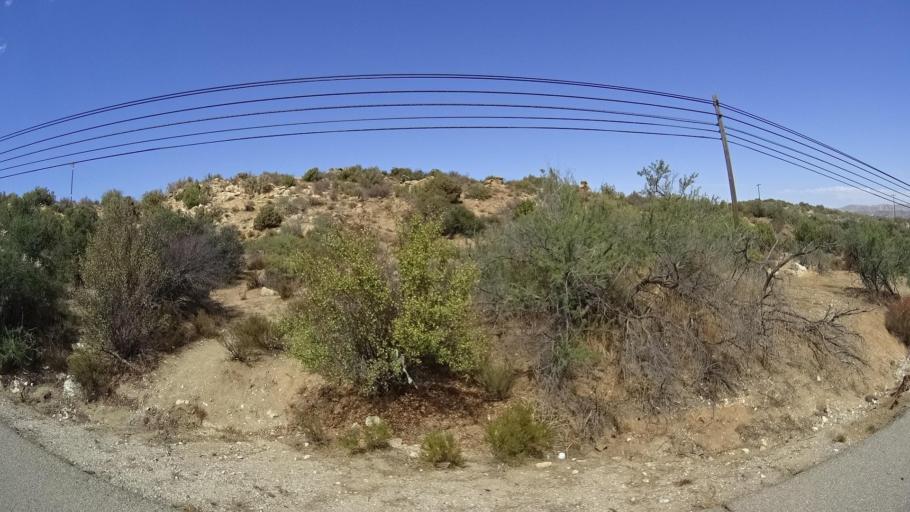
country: MX
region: Baja California
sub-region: Tecate
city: Cereso del Hongo
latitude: 32.6149
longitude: -116.2112
